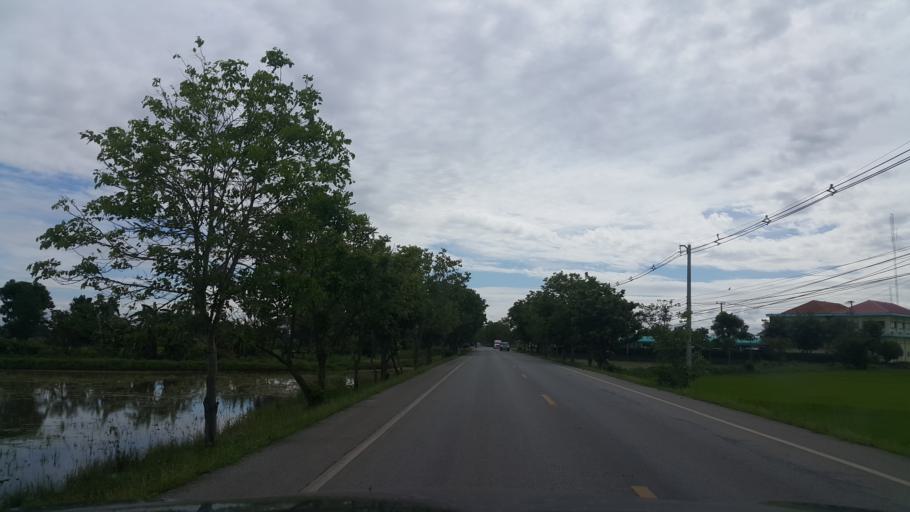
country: TH
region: Uttaradit
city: Phichai
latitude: 17.2947
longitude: 100.0989
